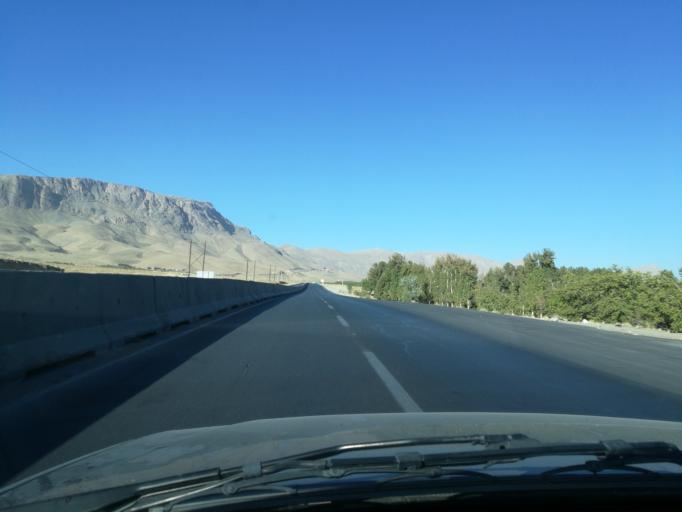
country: IR
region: Chahar Mahall va Bakhtiari
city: Farrokh Shahr
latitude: 32.3508
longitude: 51.1264
